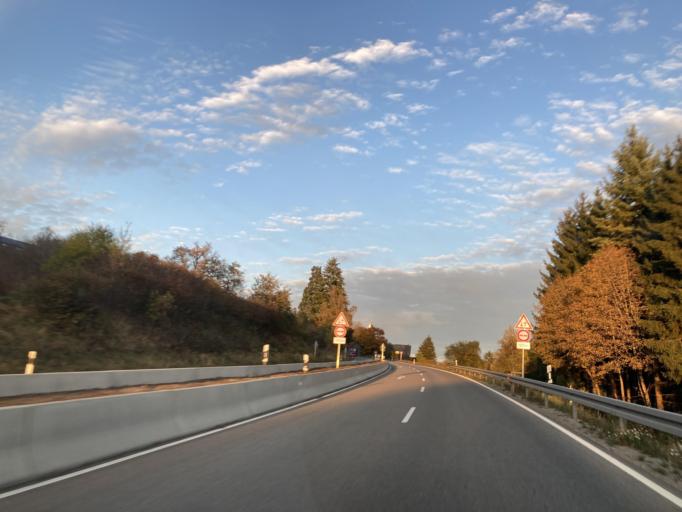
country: DE
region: Baden-Wuerttemberg
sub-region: Tuebingen Region
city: Zimmern unter der Burg
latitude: 48.1944
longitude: 8.6948
